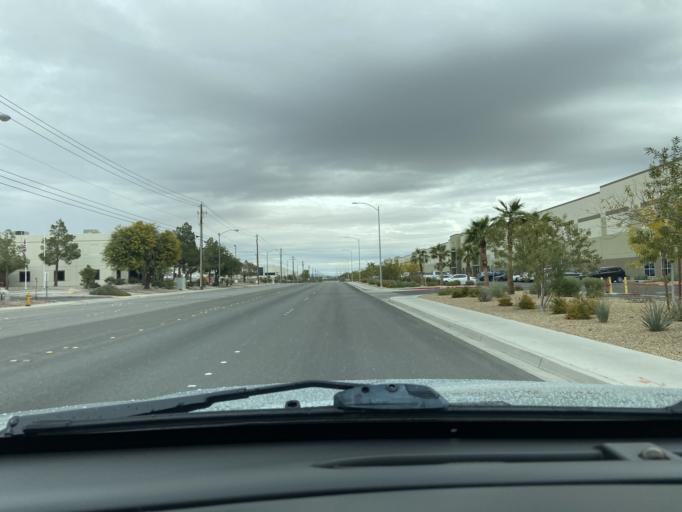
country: US
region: Nevada
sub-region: Clark County
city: North Las Vegas
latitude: 36.2469
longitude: -115.1118
